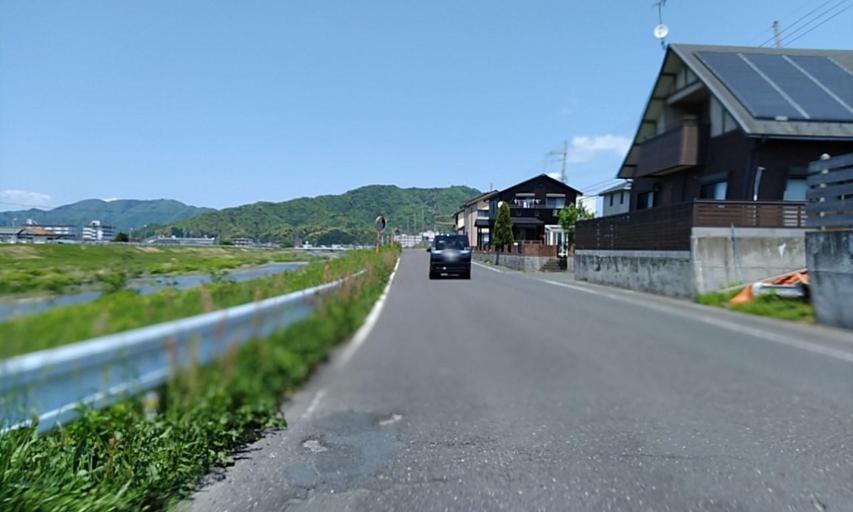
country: JP
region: Kyoto
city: Maizuru
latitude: 35.4373
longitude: 135.3359
